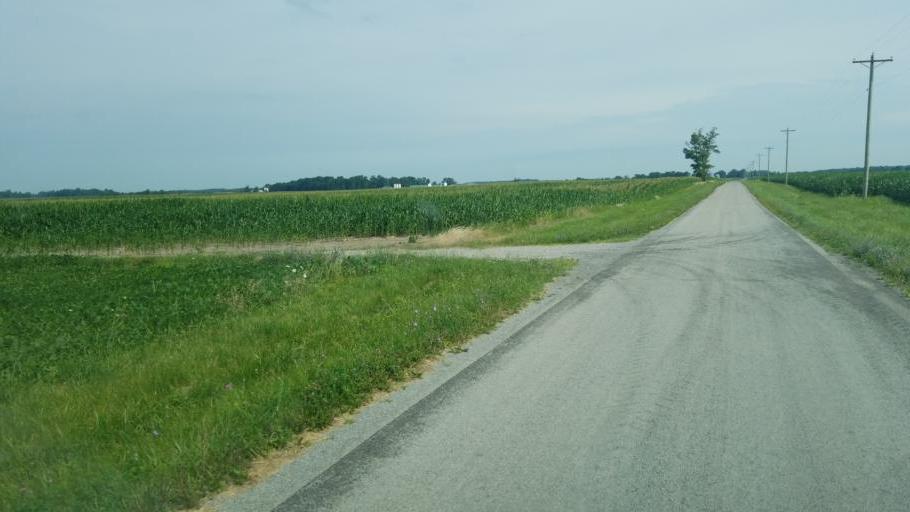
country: US
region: Ohio
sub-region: Wyandot County
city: Upper Sandusky
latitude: 40.7522
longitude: -83.3240
